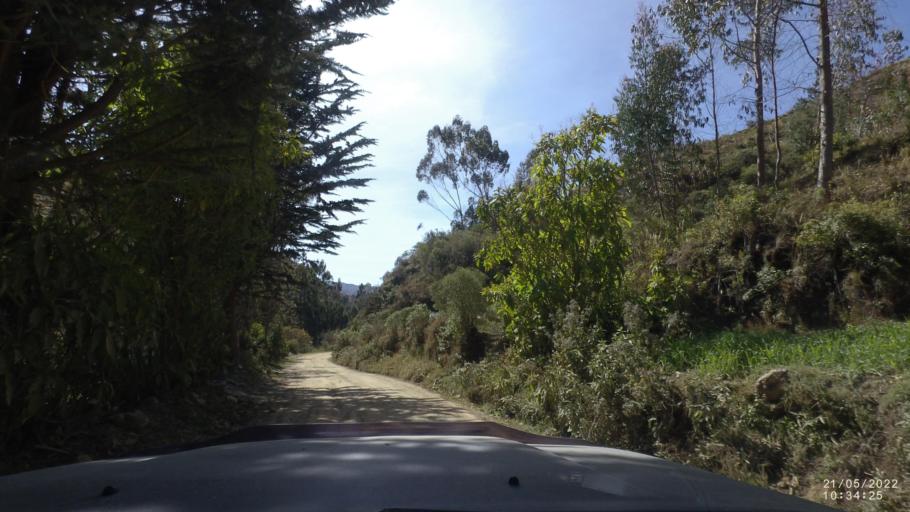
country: BO
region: Cochabamba
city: Colomi
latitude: -17.3205
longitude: -65.9315
